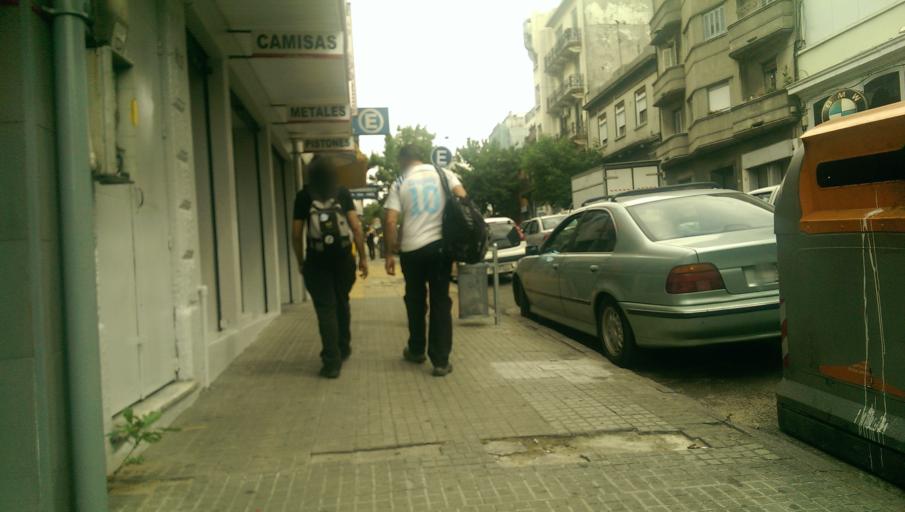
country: UY
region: Montevideo
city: Montevideo
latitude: -34.9010
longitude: -56.1884
